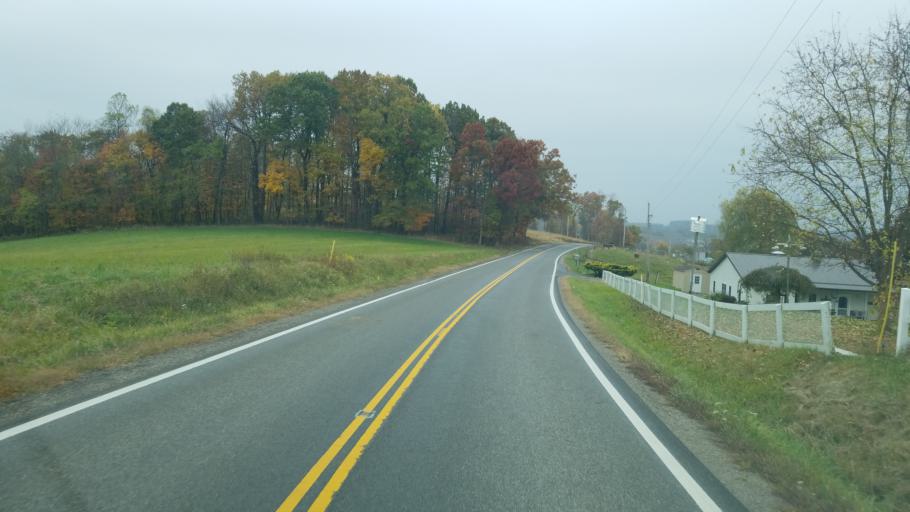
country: US
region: Ohio
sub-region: Coshocton County
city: West Lafayette
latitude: 40.4036
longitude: -81.8035
